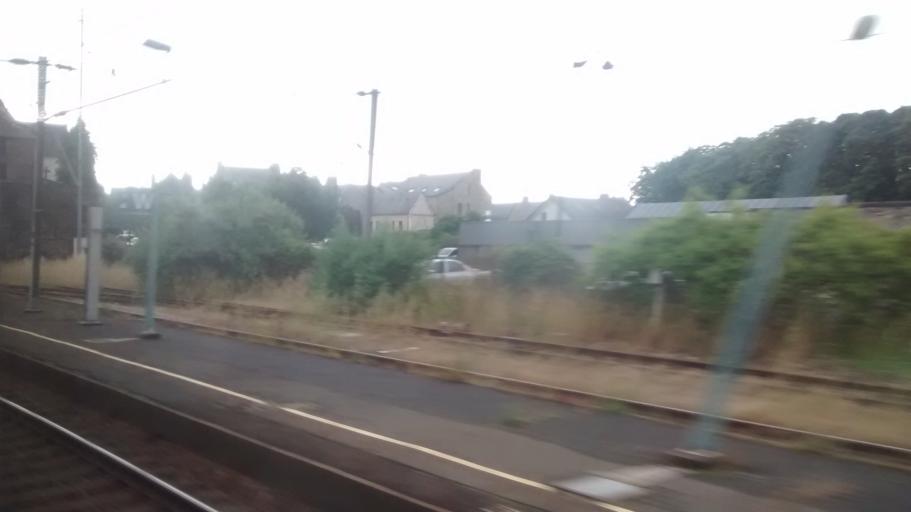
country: FR
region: Brittany
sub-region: Departement d'Ille-et-Vilaine
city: Vitre
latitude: 48.1225
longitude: -1.2146
